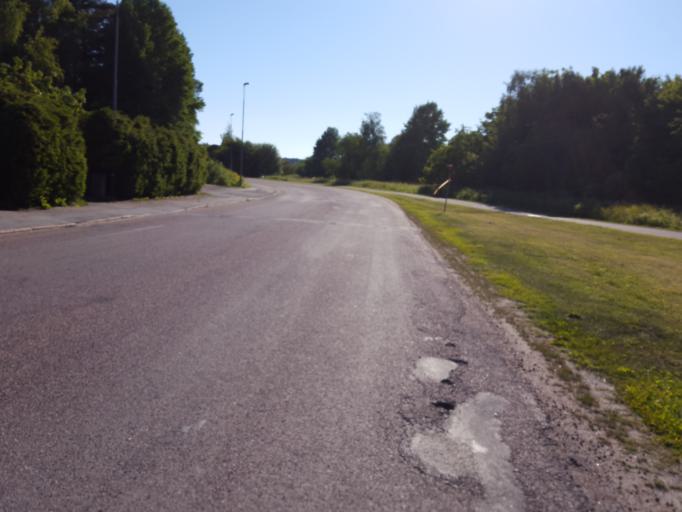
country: SE
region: Uppsala
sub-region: Uppsala Kommun
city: Uppsala
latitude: 59.8447
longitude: 17.6057
